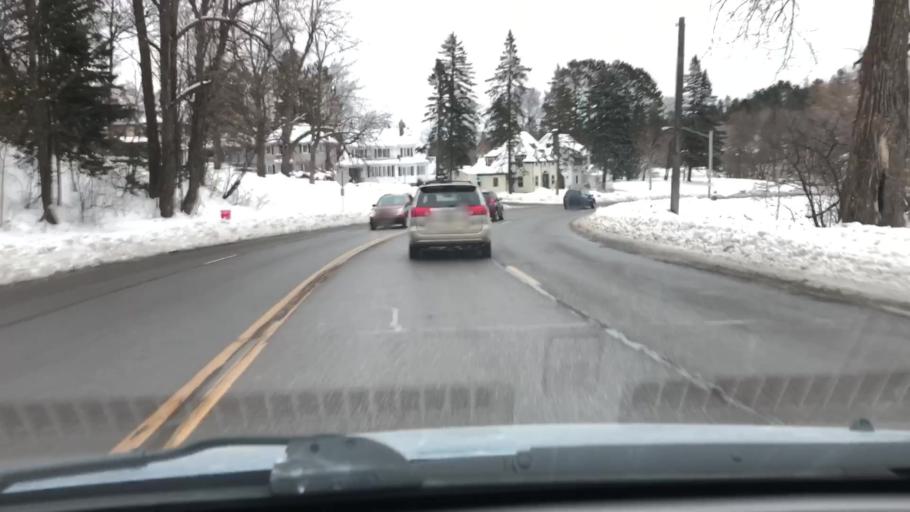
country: US
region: Minnesota
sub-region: Saint Louis County
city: Arnold
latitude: 46.8385
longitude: -92.0773
